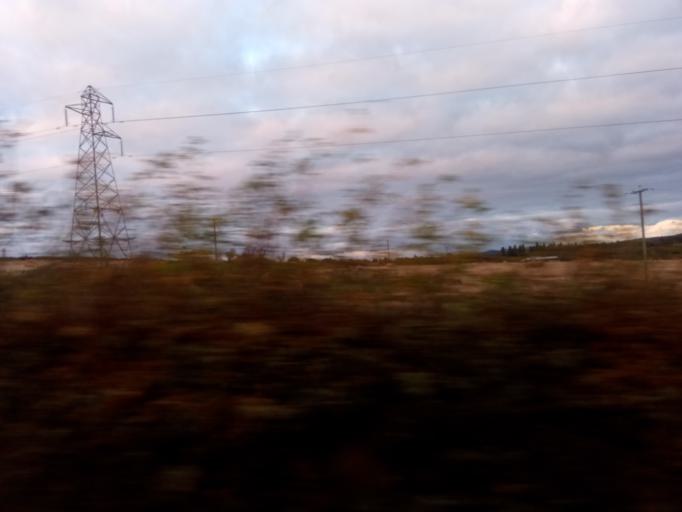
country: GB
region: Scotland
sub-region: Fife
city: Pathhead
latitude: 55.8728
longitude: -2.9959
